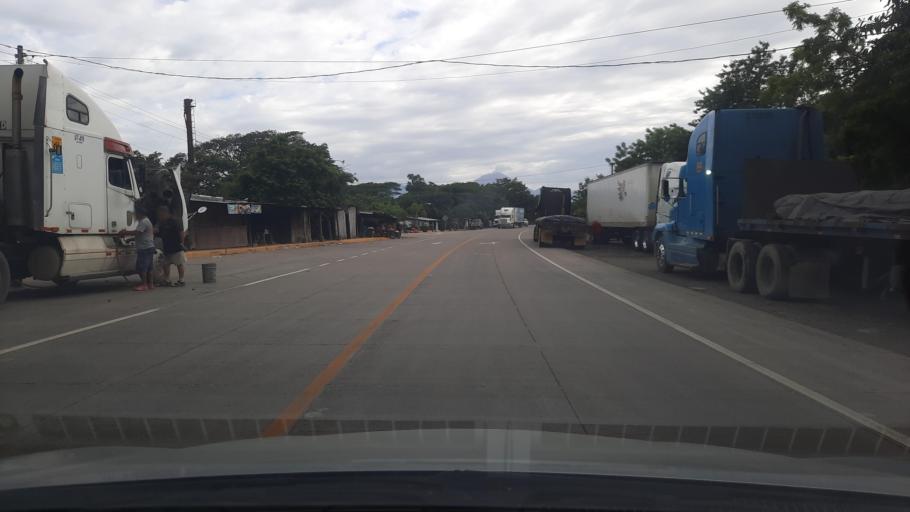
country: NI
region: Chinandega
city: Somotillo
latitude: 12.8622
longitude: -86.8526
